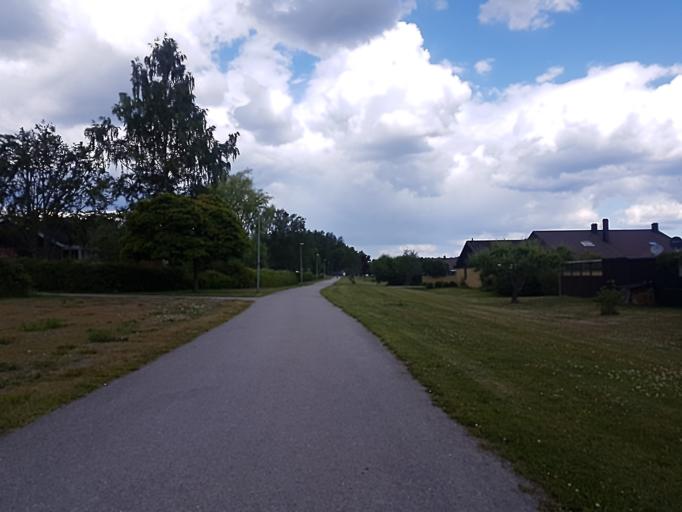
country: SE
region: Soedermanland
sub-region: Gnesta Kommun
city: Gnesta
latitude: 59.0368
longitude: 17.3276
